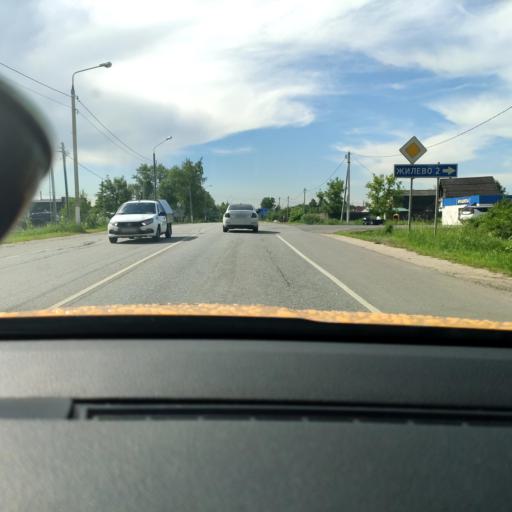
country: RU
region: Moskovskaya
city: Zhilevo
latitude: 54.9659
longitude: 37.9817
